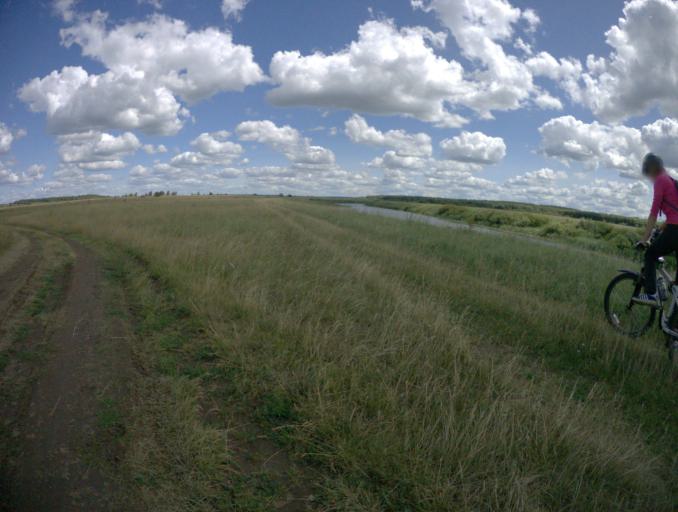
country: RU
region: Vladimir
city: Orgtrud
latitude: 56.3008
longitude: 40.6185
